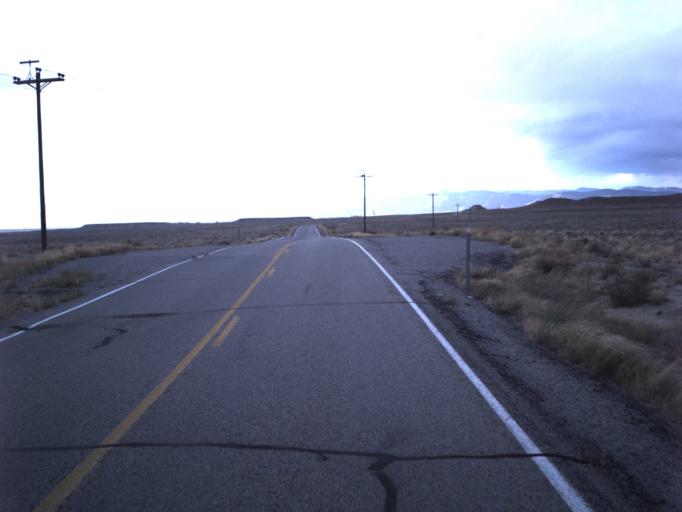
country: US
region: Utah
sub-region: Grand County
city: Moab
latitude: 38.9144
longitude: -109.3271
